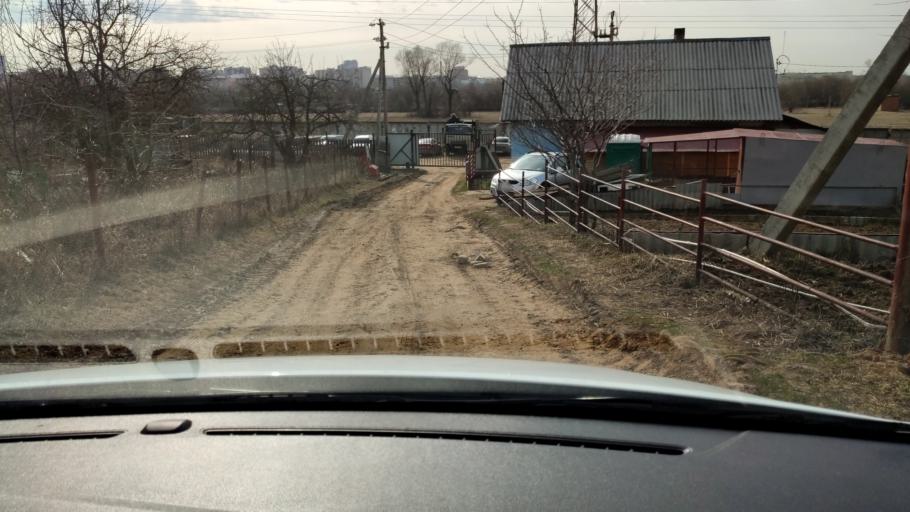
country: RU
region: Tatarstan
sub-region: Gorod Kazan'
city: Kazan
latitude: 55.8194
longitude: 49.2114
